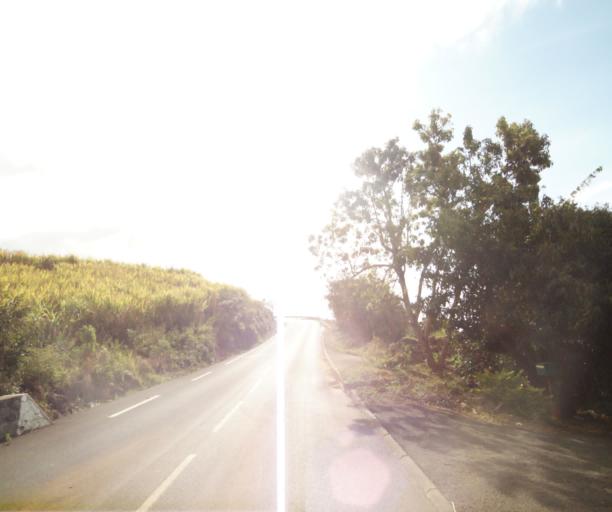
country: RE
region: Reunion
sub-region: Reunion
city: Saint-Paul
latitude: -21.0227
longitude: 55.3128
